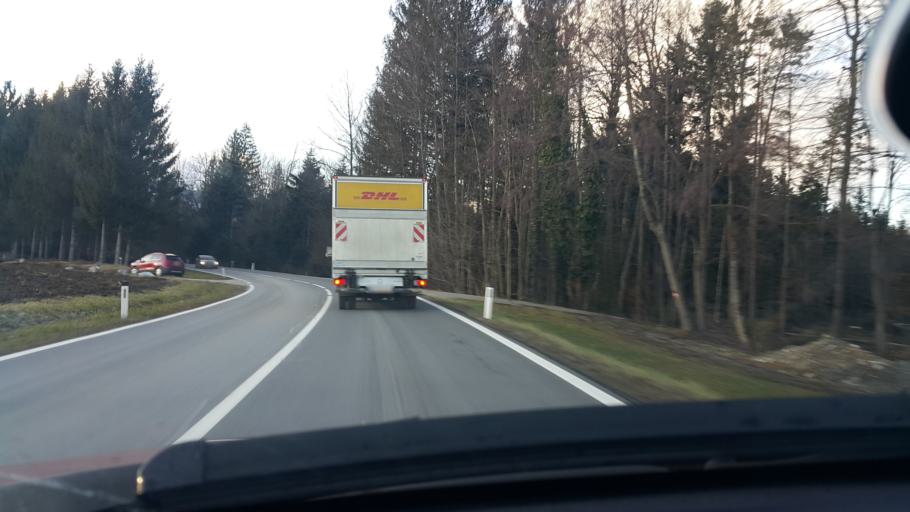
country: AT
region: Styria
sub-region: Politischer Bezirk Deutschlandsberg
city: Hollenegg
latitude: 46.7972
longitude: 15.2299
